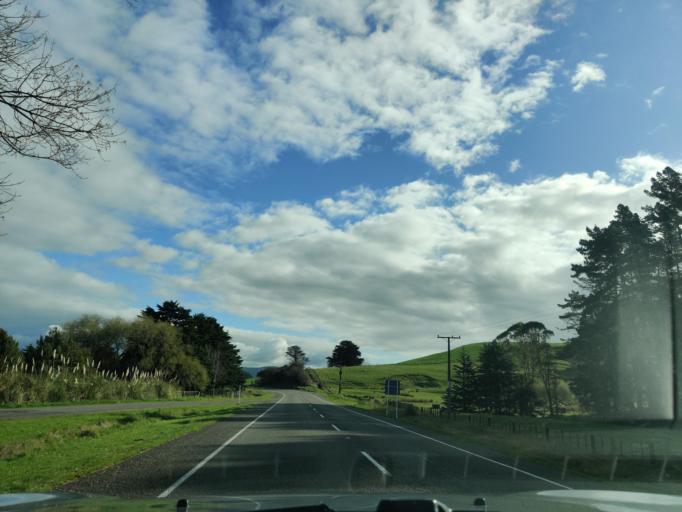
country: NZ
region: Manawatu-Wanganui
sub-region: Palmerston North City
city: Palmerston North
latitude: -40.3386
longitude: 175.8915
